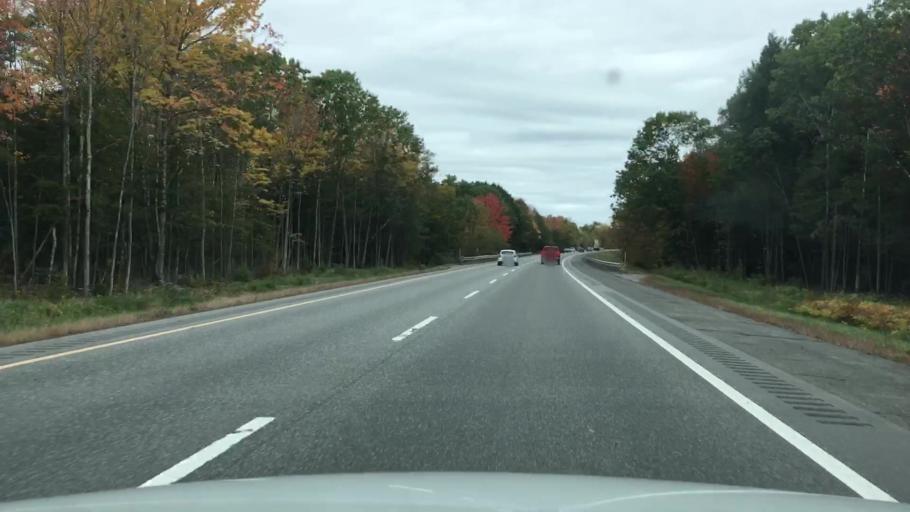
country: US
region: Maine
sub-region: Kennebec County
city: Oakland
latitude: 44.5133
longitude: -69.7020
